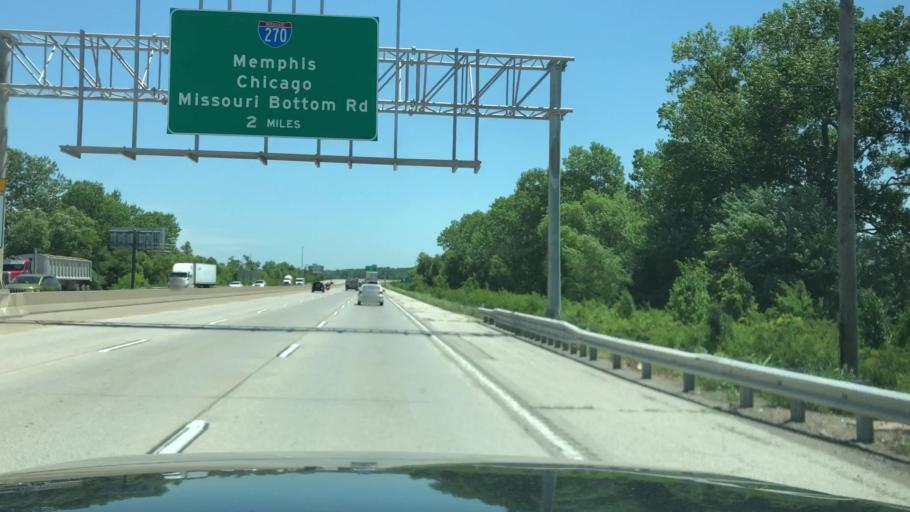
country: US
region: Missouri
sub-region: Saint Louis County
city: Bridgeton
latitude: 38.7905
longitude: -90.4336
